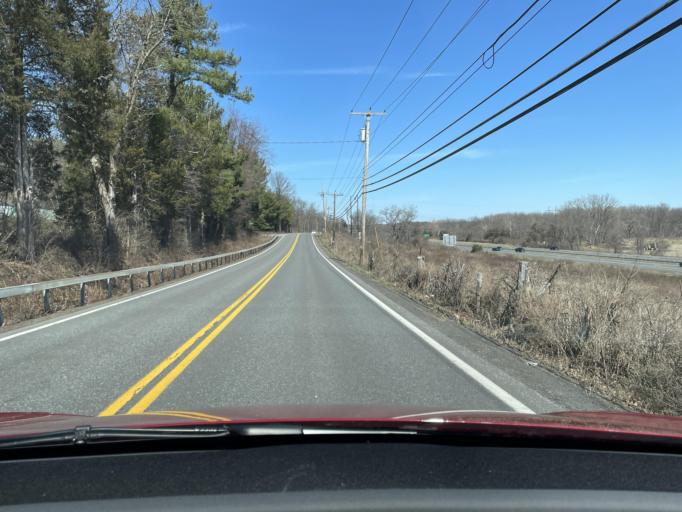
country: US
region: New York
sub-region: Ulster County
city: Lincoln Park
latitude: 41.9642
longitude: -74.0162
